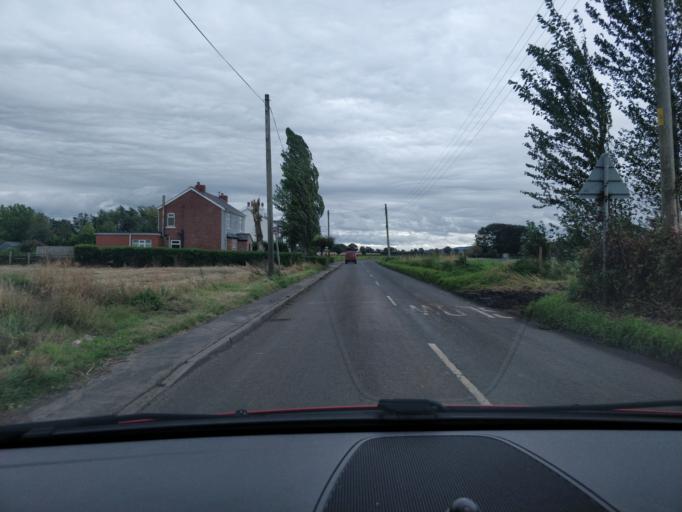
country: GB
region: England
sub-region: Lancashire
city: Ormskirk
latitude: 53.6179
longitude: -2.8481
